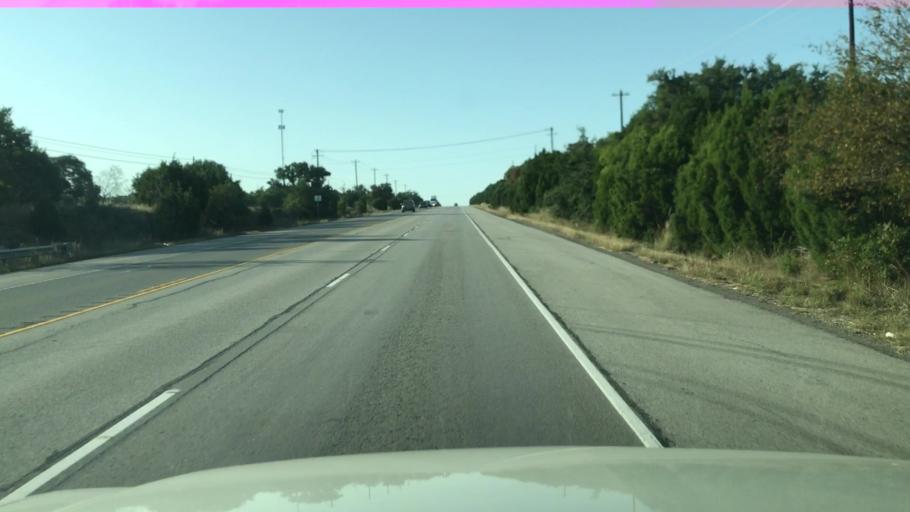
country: US
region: Texas
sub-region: Blanco County
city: Blanco
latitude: 30.1808
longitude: -98.3795
